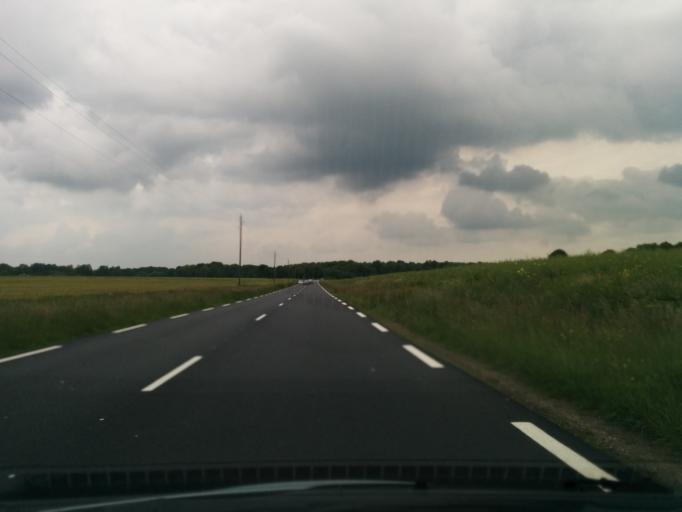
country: FR
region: Ile-de-France
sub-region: Departement des Yvelines
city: Limetz-Villez
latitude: 49.1391
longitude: 1.5275
